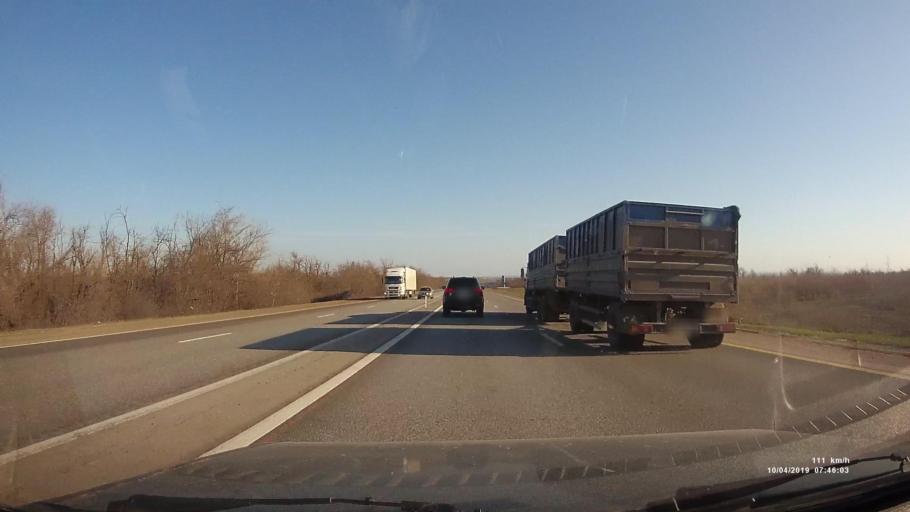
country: RU
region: Rostov
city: Likhoy
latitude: 48.2004
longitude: 40.2678
